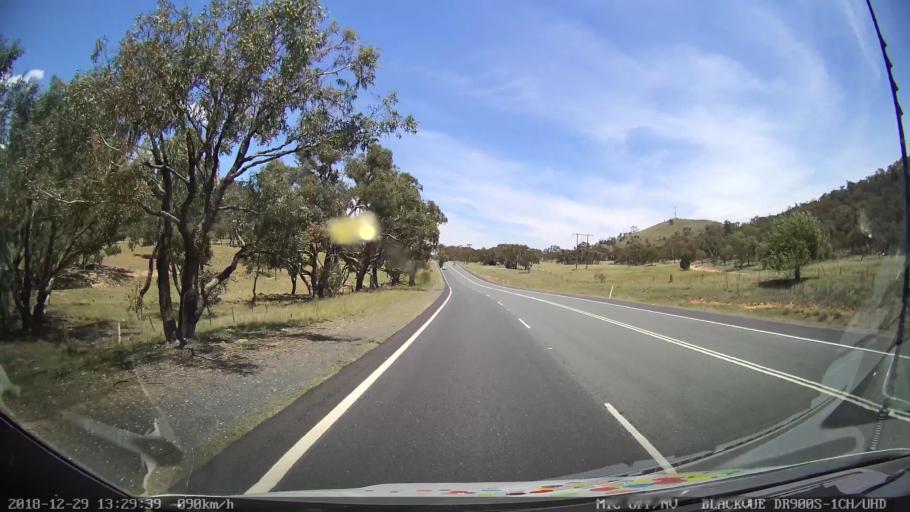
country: AU
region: New South Wales
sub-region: Cooma-Monaro
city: Cooma
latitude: -35.8931
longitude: 149.1613
